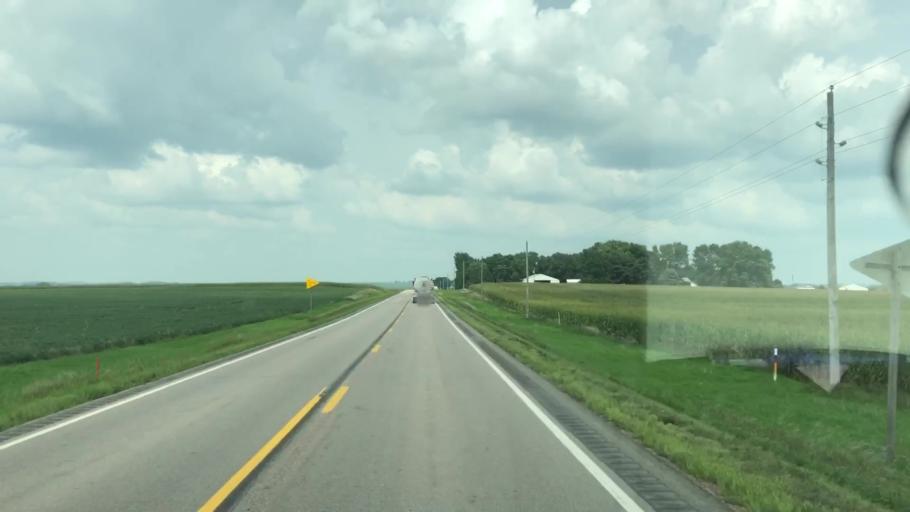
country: US
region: Iowa
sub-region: Plymouth County
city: Remsen
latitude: 42.7946
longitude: -95.9577
